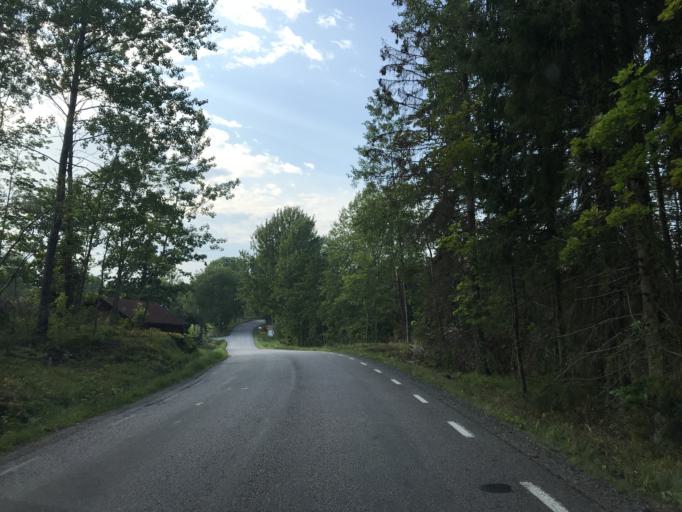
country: SE
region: Stockholm
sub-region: Norrtalje Kommun
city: Bjorko
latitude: 59.8695
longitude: 19.0161
